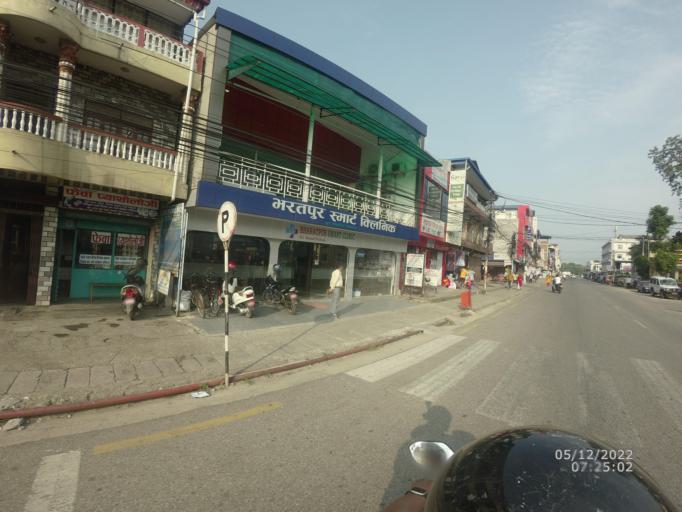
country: NP
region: Central Region
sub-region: Narayani Zone
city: Bharatpur
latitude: 27.6809
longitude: 84.4331
